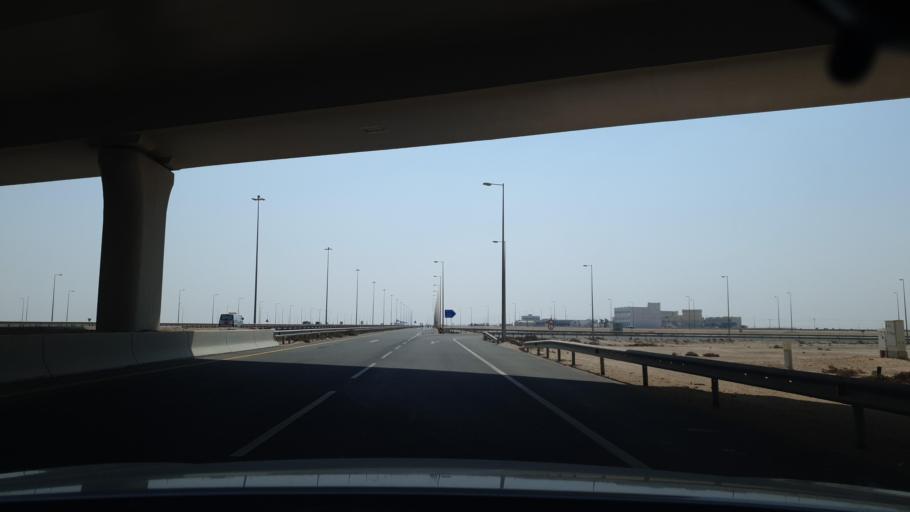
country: QA
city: Al Ghuwayriyah
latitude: 25.8291
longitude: 51.3496
